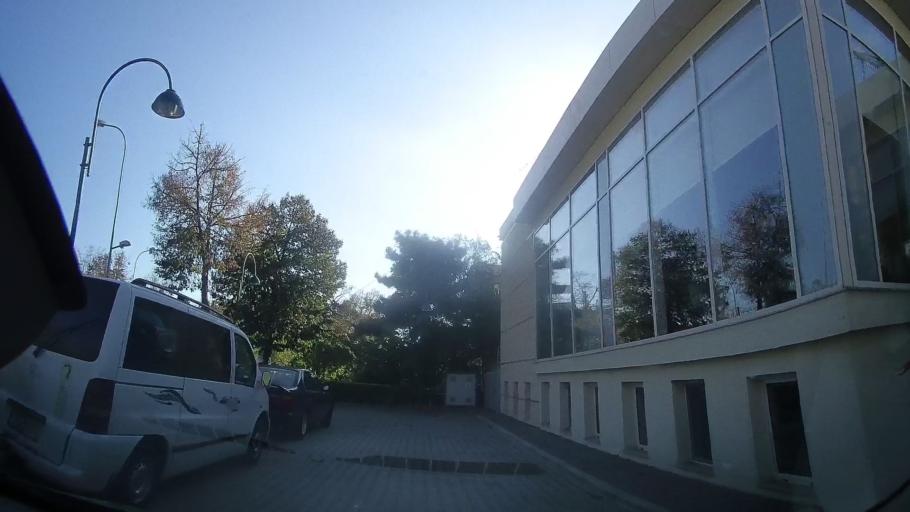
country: RO
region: Constanta
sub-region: Comuna Douazeci si Trei August
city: Douazeci si Trei August
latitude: 43.8800
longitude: 28.6029
